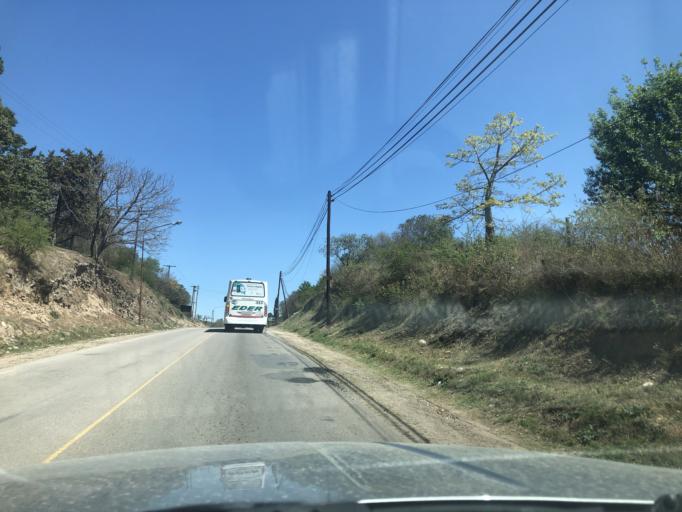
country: AR
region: Cordoba
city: La Granja
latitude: -31.0164
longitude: -64.2724
